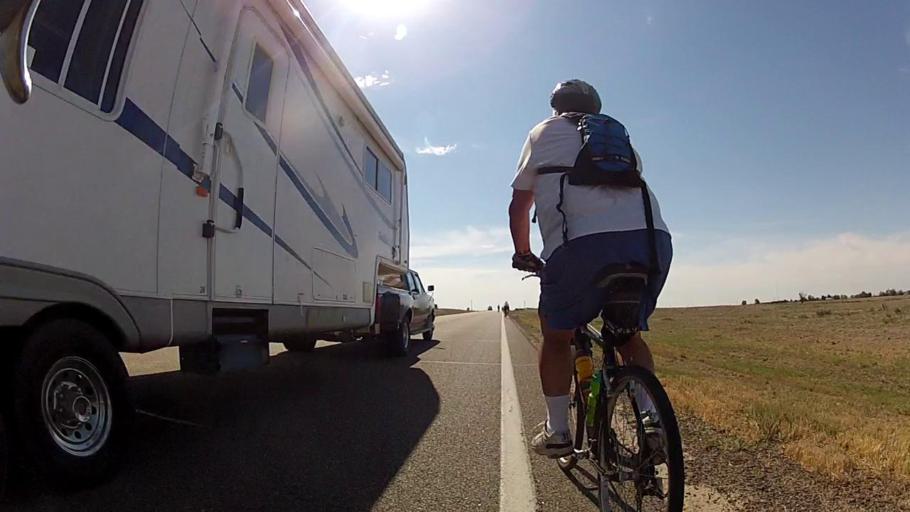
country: US
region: Kansas
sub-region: Grant County
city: Ulysses
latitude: 37.5677
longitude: -101.3213
